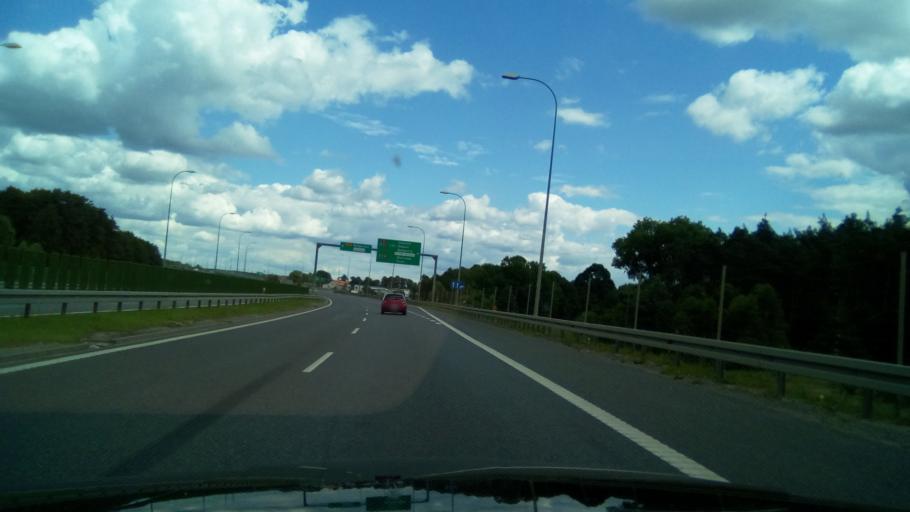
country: PL
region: Kujawsko-Pomorskie
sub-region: Powiat bydgoski
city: Biale Blota
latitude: 53.0887
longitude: 17.8865
